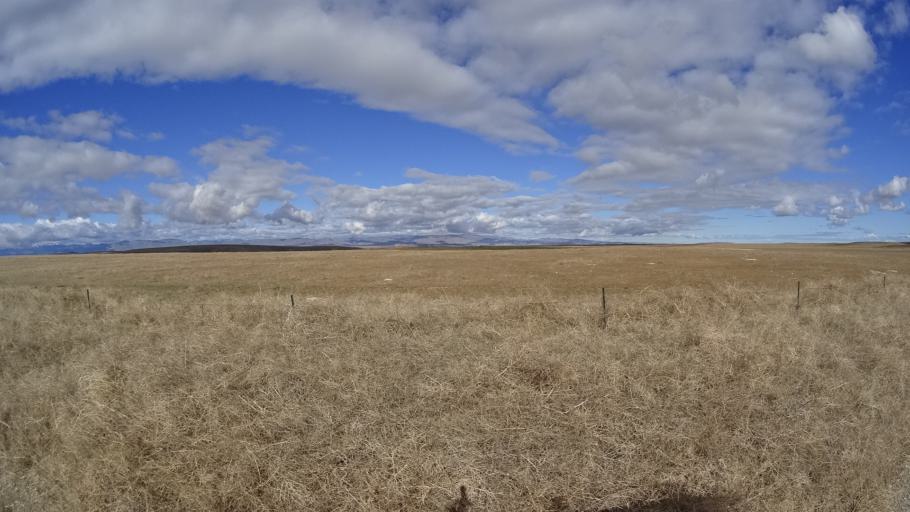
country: US
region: Idaho
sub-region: Owyhee County
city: Murphy
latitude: 43.2942
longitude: -116.3942
